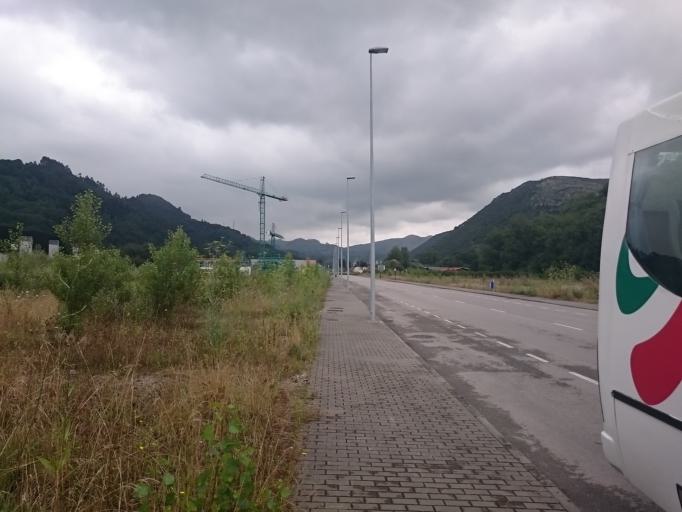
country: ES
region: Asturias
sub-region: Province of Asturias
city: Oviedo
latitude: 43.3220
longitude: -5.7993
